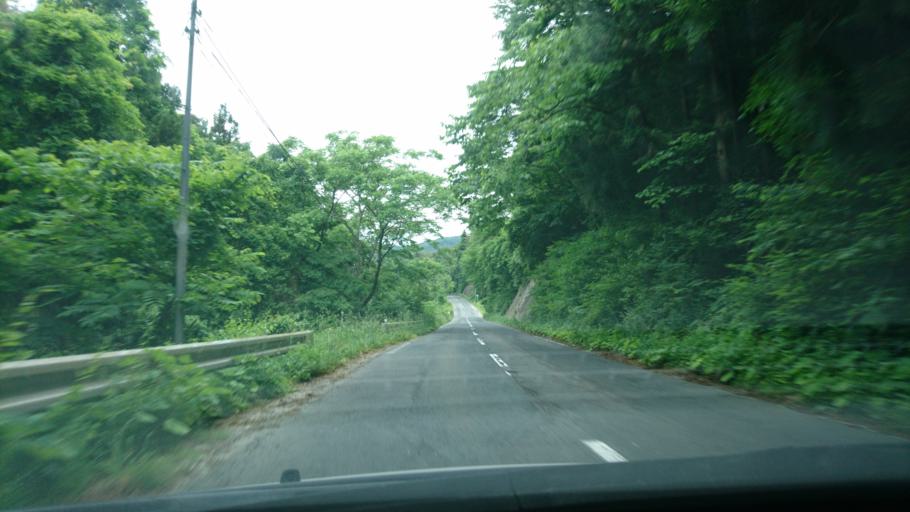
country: JP
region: Iwate
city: Ichinoseki
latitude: 38.9480
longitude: 141.2663
